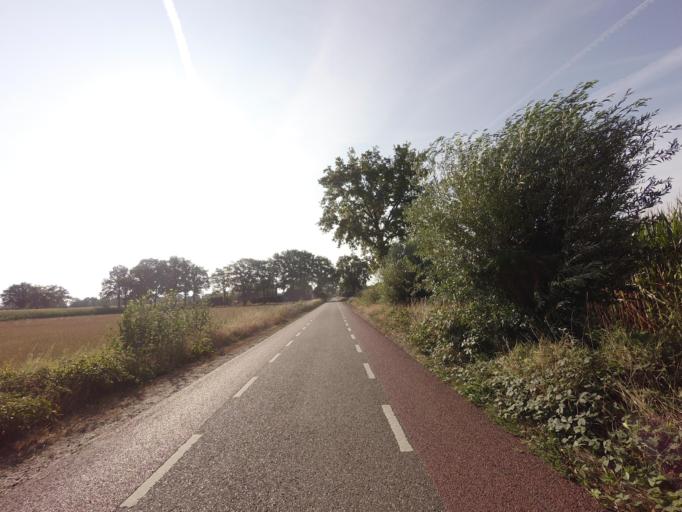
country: NL
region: North Brabant
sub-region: Gemeente Landerd
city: Zeeland
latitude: 51.6806
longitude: 5.6969
